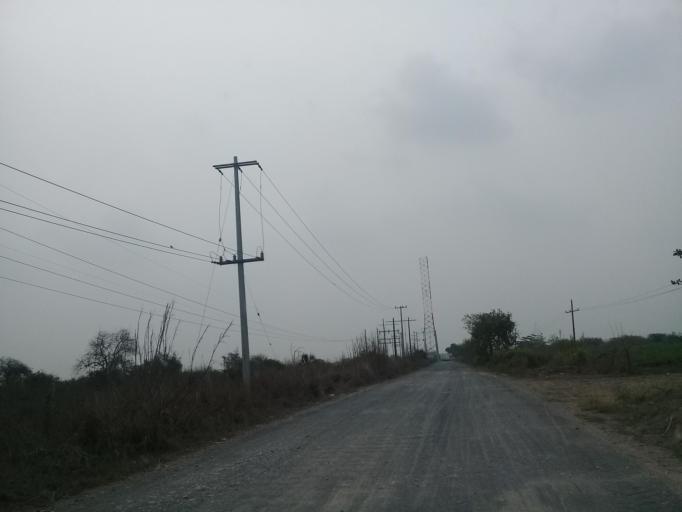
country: MX
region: Veracruz
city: Paso del Toro
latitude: 18.9101
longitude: -96.1960
